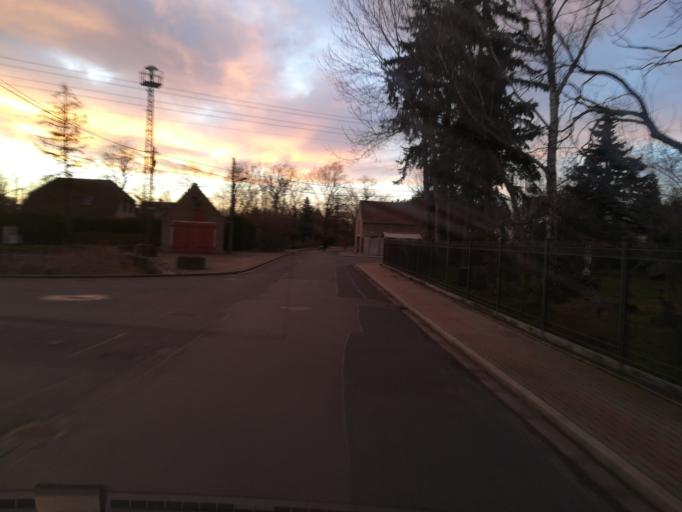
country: DE
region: Saxony-Anhalt
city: Brehna
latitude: 51.5388
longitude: 12.2266
